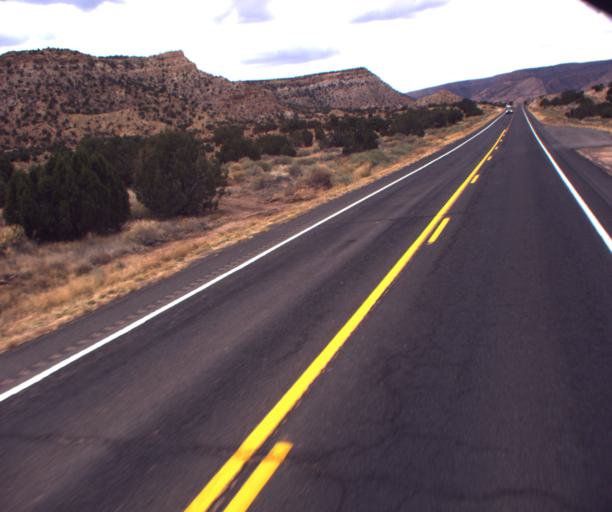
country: US
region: Arizona
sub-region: Navajo County
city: Kayenta
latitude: 36.6966
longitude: -110.3464
